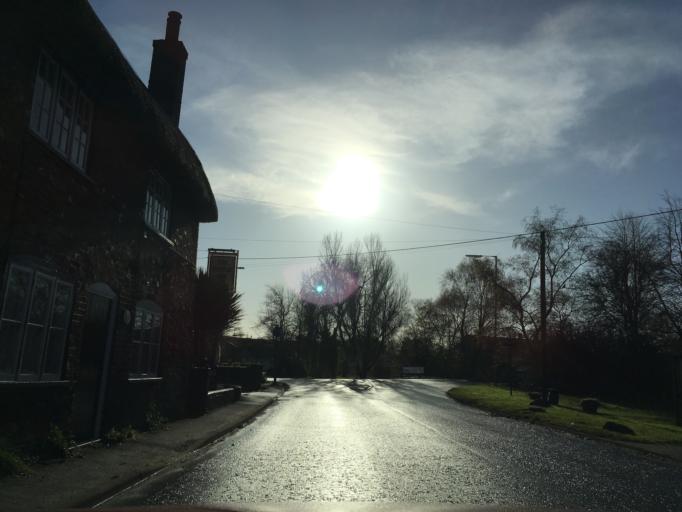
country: GB
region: England
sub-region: Wiltshire
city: Collingbourne Kingston
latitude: 51.2828
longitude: -1.6519
